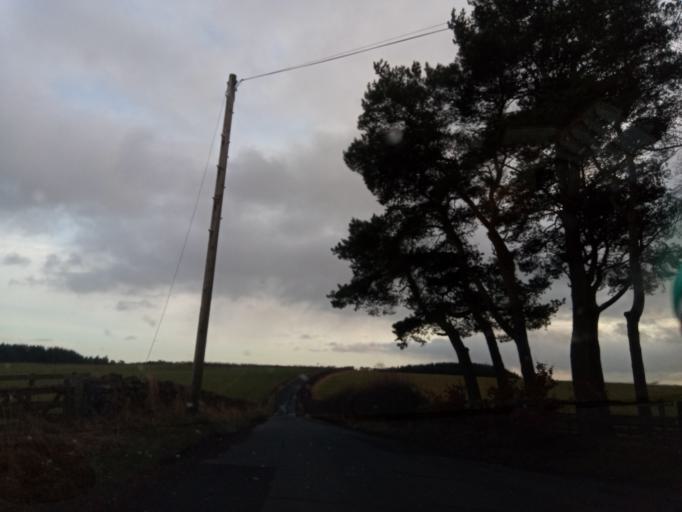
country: GB
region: Scotland
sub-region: The Scottish Borders
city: Selkirk
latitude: 55.5586
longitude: -2.7866
